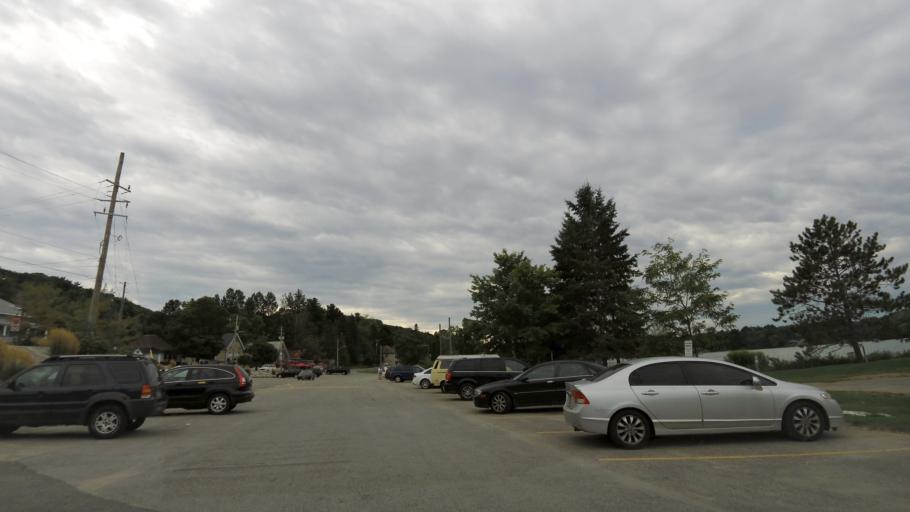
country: CA
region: Ontario
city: Bancroft
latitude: 45.0461
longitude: -78.5117
